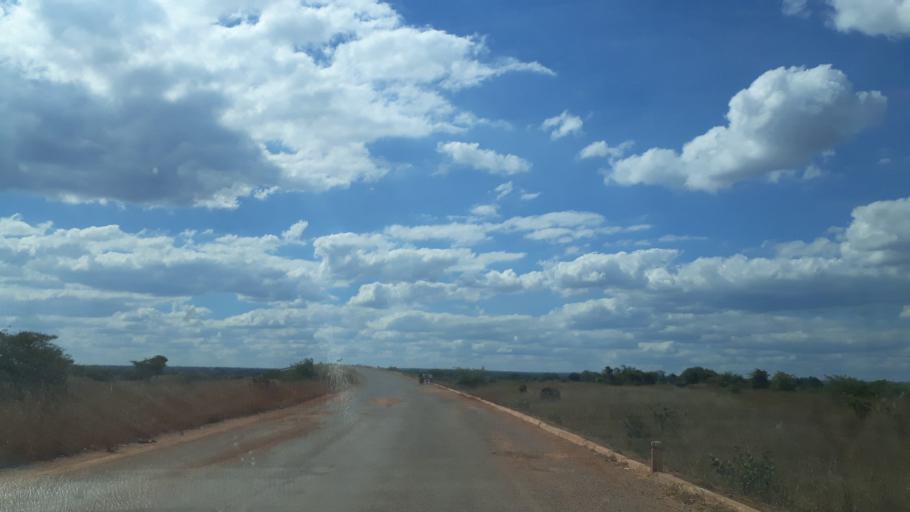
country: ZM
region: Copperbelt
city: Mufulira
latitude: -11.9893
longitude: 28.7303
